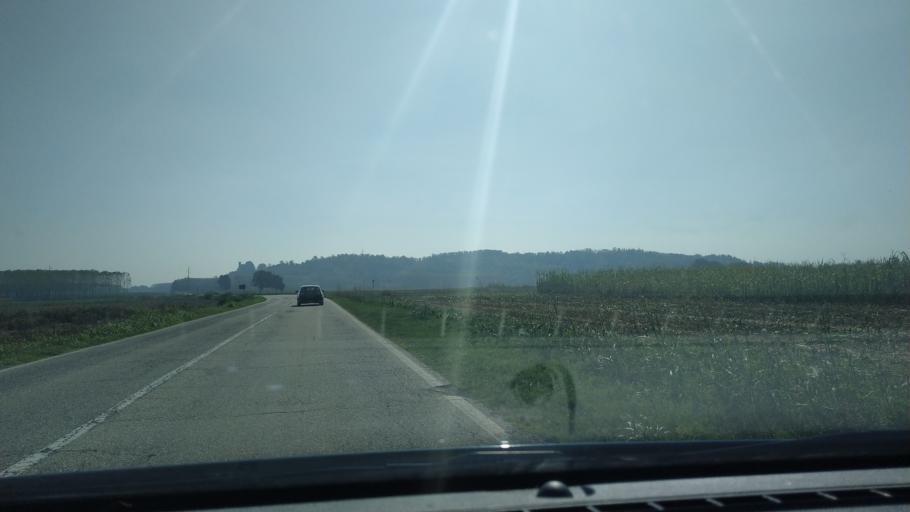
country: IT
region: Piedmont
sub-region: Provincia di Alessandria
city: Giarole
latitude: 45.0725
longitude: 8.5781
